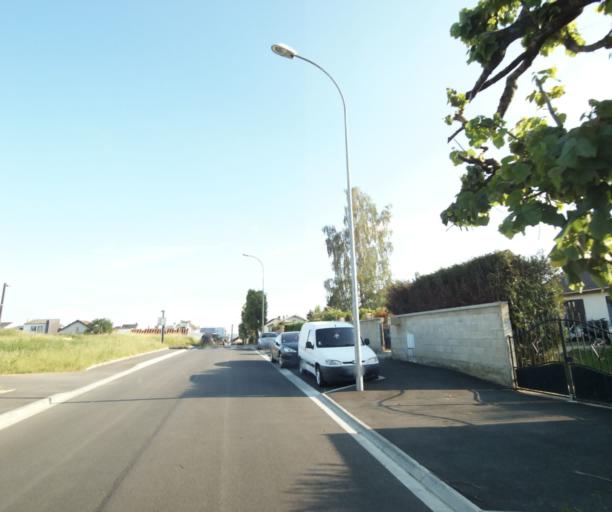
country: FR
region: Champagne-Ardenne
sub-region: Departement des Ardennes
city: Charleville-Mezieres
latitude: 49.7893
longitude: 4.7097
